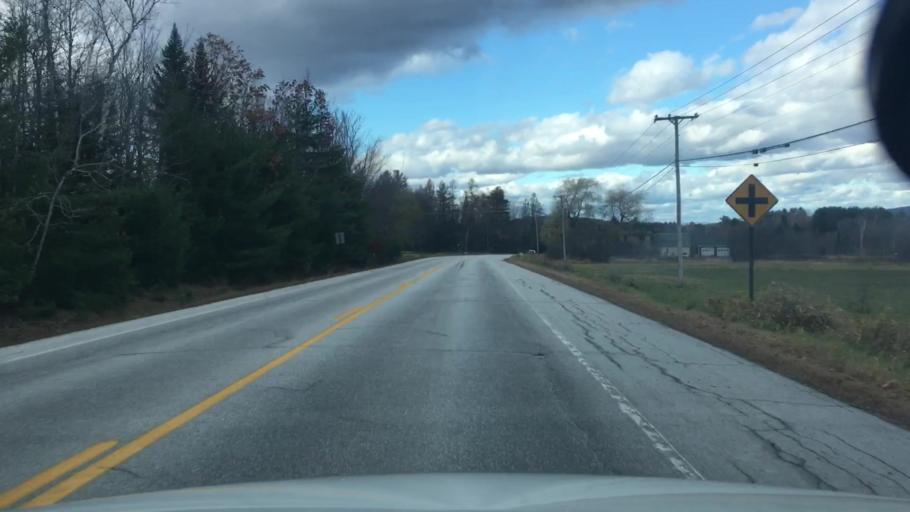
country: US
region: Maine
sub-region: Somerset County
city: Saint Albans
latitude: 44.8537
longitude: -69.4396
